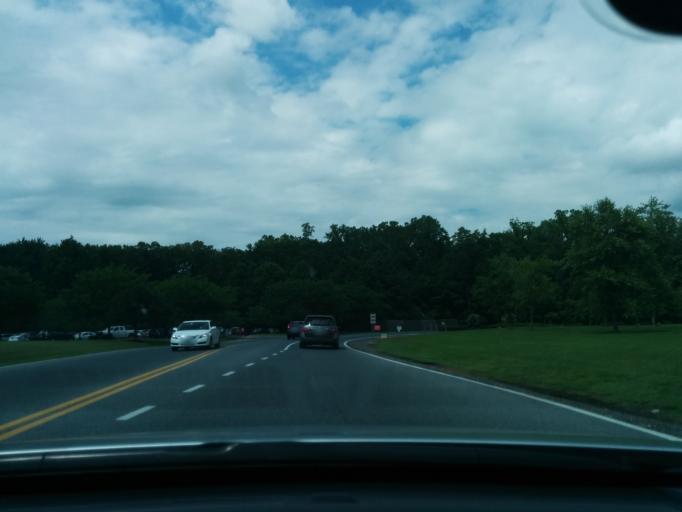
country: US
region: Maryland
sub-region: Worcester County
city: Ocean Pines
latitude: 38.3795
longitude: -75.1656
